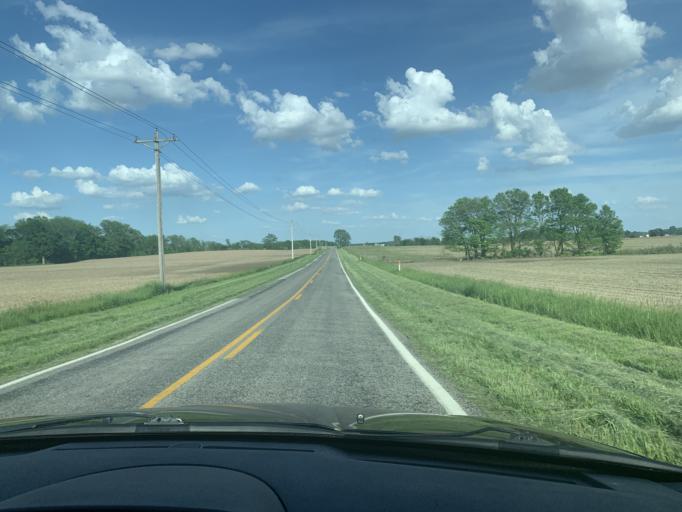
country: US
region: Ohio
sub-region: Logan County
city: De Graff
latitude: 40.2403
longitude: -83.9495
